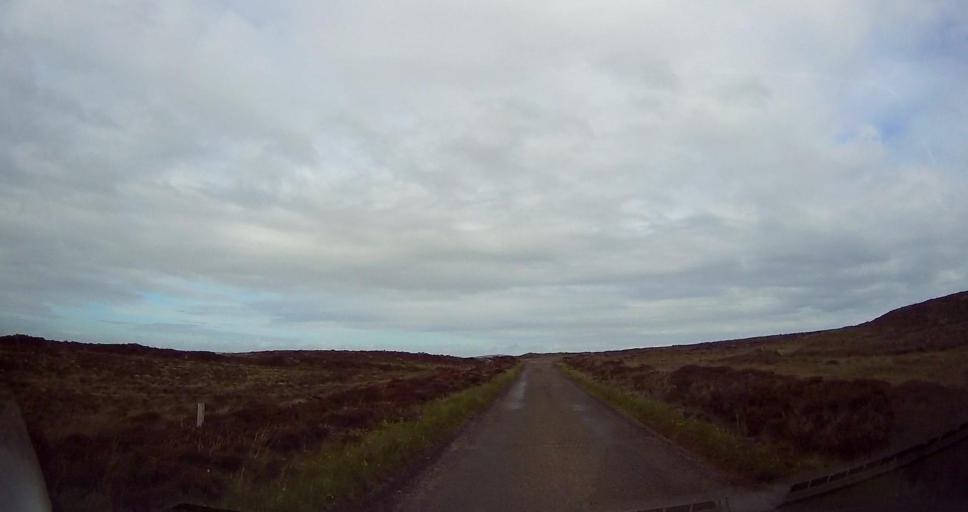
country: GB
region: Scotland
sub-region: Orkney Islands
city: Stromness
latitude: 58.9030
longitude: -3.3039
